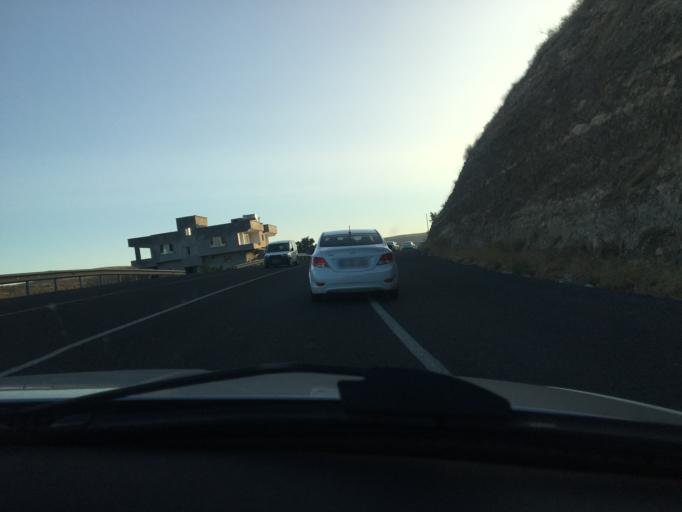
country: TR
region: Sanliurfa
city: Halfeti
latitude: 37.2045
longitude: 37.9708
